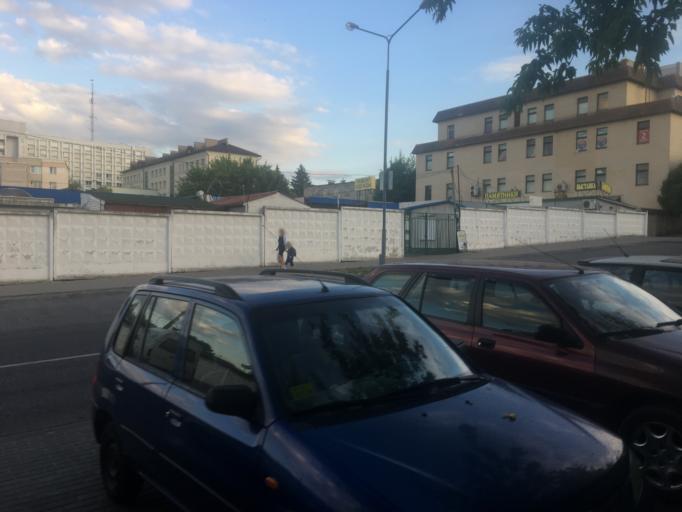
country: BY
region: Grodnenskaya
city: Hrodna
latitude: 53.6939
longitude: 23.8248
